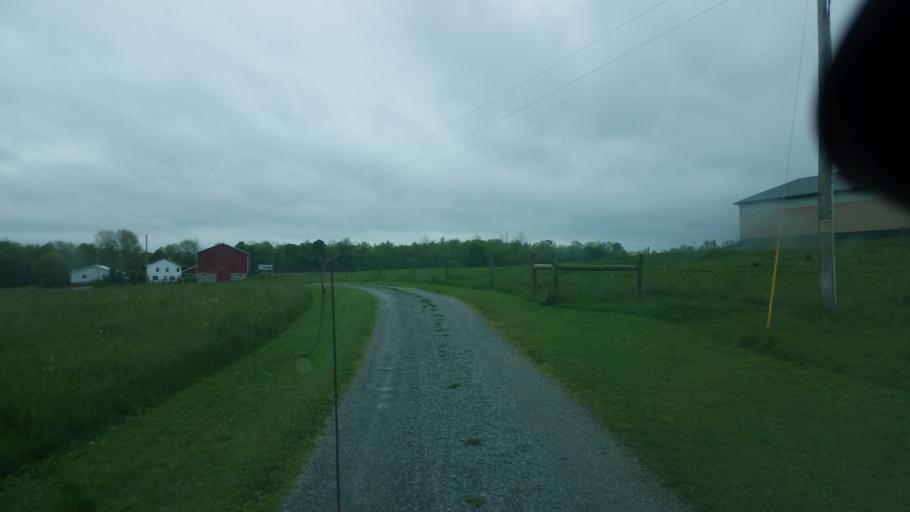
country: US
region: Ohio
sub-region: Highland County
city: Leesburg
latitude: 39.2594
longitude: -83.5429
